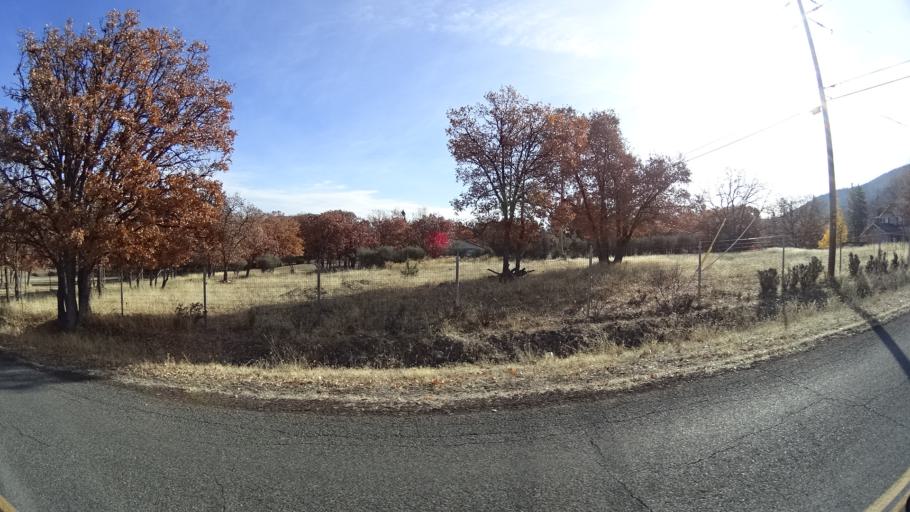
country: US
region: California
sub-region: Siskiyou County
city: Yreka
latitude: 41.6648
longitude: -122.6209
